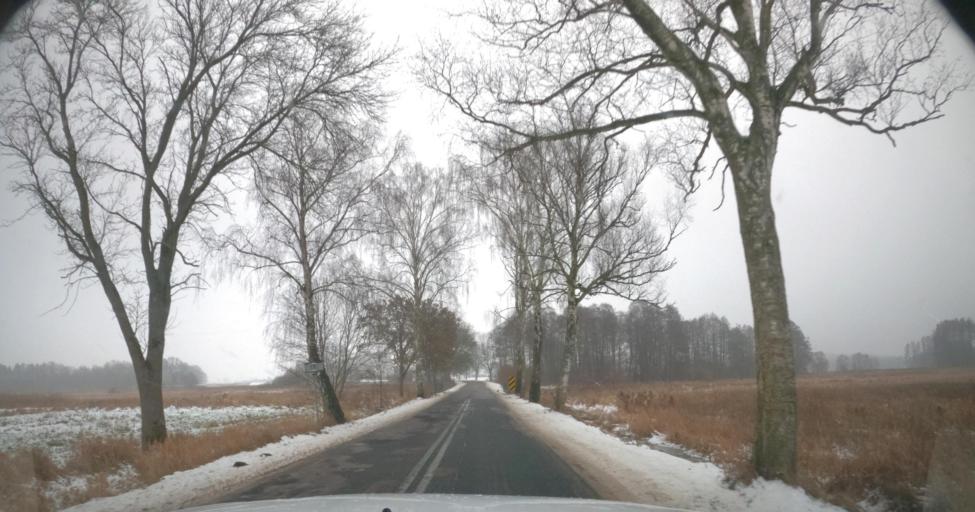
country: PL
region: West Pomeranian Voivodeship
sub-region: Powiat gryficki
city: Brojce
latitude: 53.8991
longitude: 15.3012
